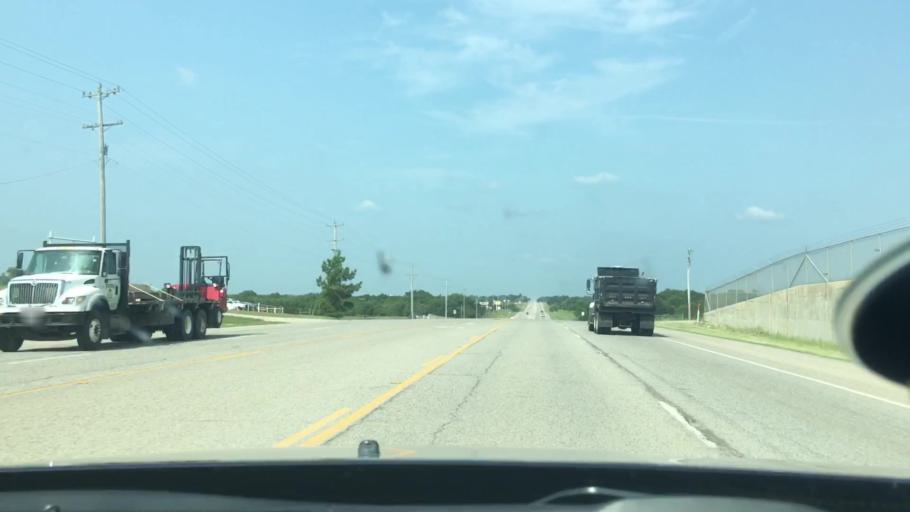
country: US
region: Oklahoma
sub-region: Bryan County
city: Calera
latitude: 33.9982
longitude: -96.4714
